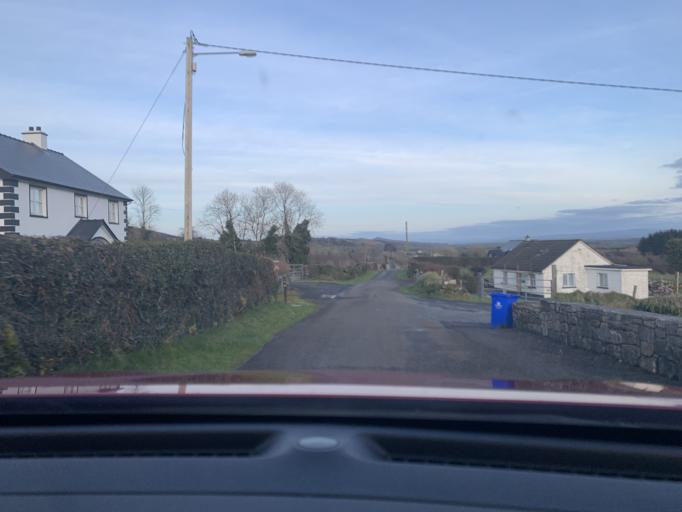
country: IE
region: Connaught
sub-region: Sligo
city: Strandhill
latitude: 54.1774
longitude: -8.6252
